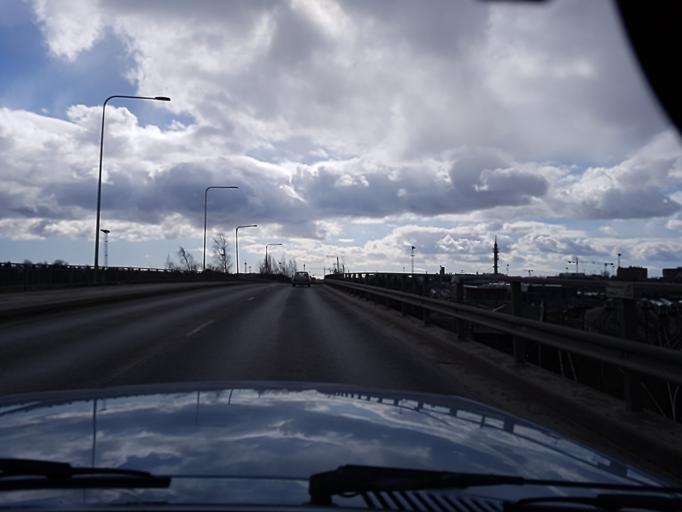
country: FI
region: Uusimaa
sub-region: Helsinki
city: Helsinki
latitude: 60.2177
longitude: 24.9338
